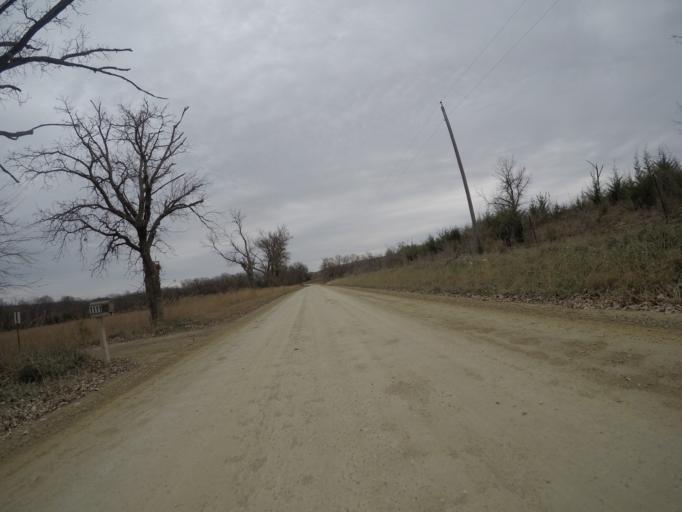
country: US
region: Kansas
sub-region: Riley County
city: Ogden
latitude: 39.1913
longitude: -96.6630
